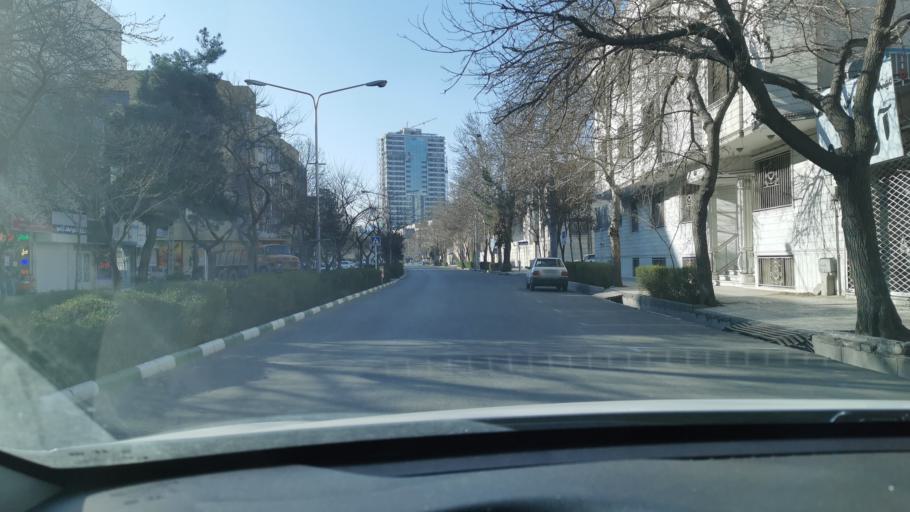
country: IR
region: Razavi Khorasan
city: Mashhad
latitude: 36.2884
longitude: 59.5673
